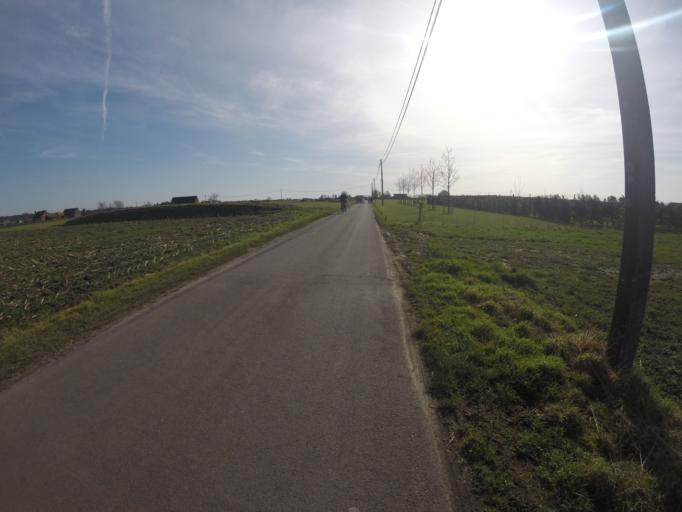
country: BE
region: Flanders
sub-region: Provincie West-Vlaanderen
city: Wingene
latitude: 51.0880
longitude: 3.2665
